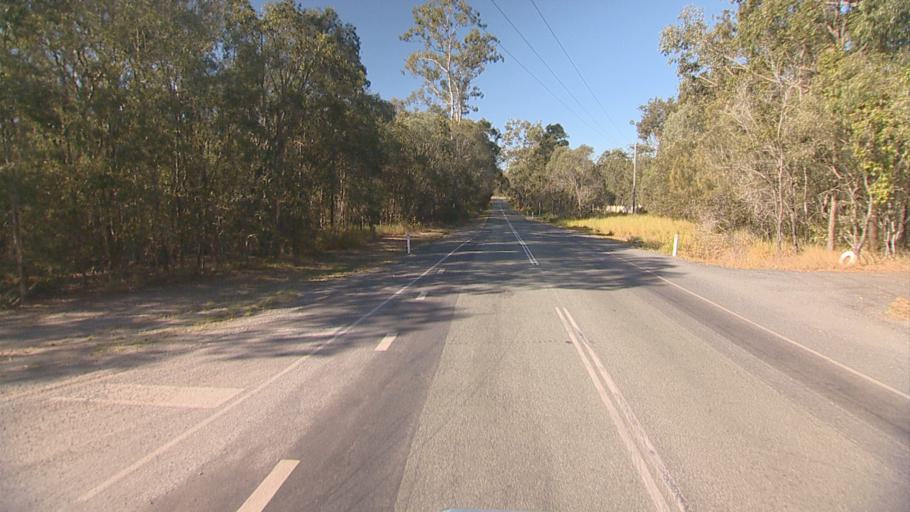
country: AU
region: Queensland
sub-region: Logan
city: North Maclean
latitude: -27.7913
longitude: 153.0380
